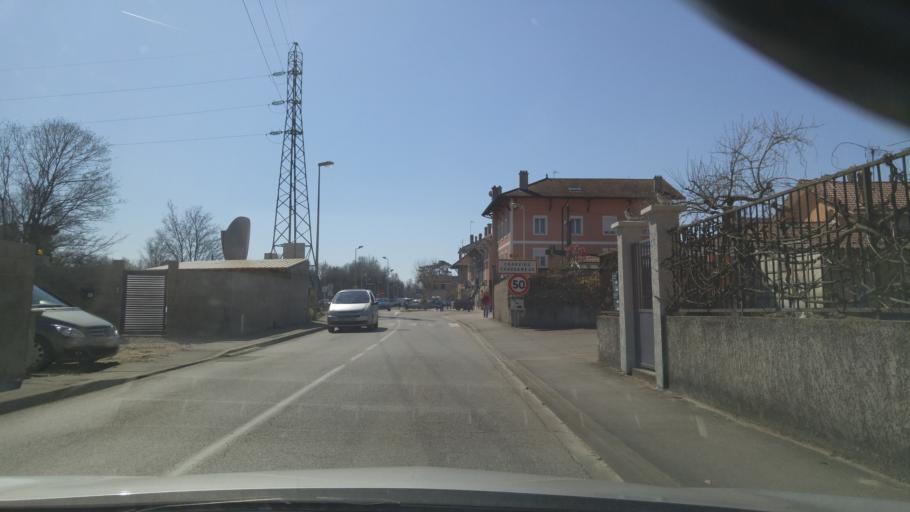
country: FR
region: Rhone-Alpes
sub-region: Departement de l'Isere
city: Tignieu-Jameyzieu
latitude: 45.7471
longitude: 5.1678
